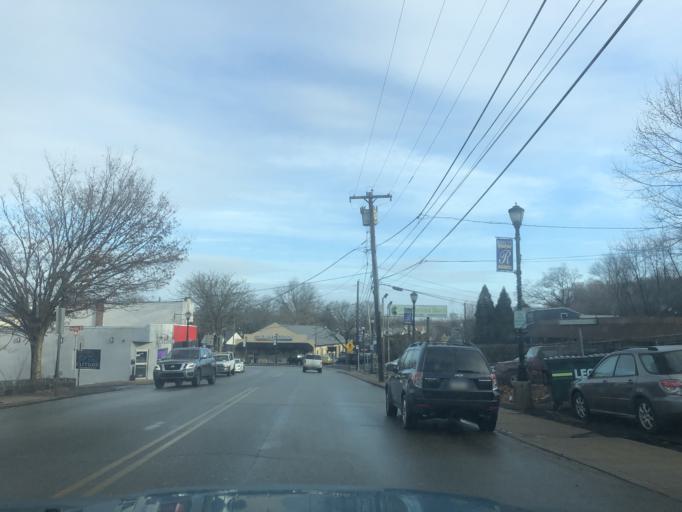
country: US
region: Pennsylvania
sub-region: Montgomery County
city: Jenkintown
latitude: 40.1219
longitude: -75.1329
